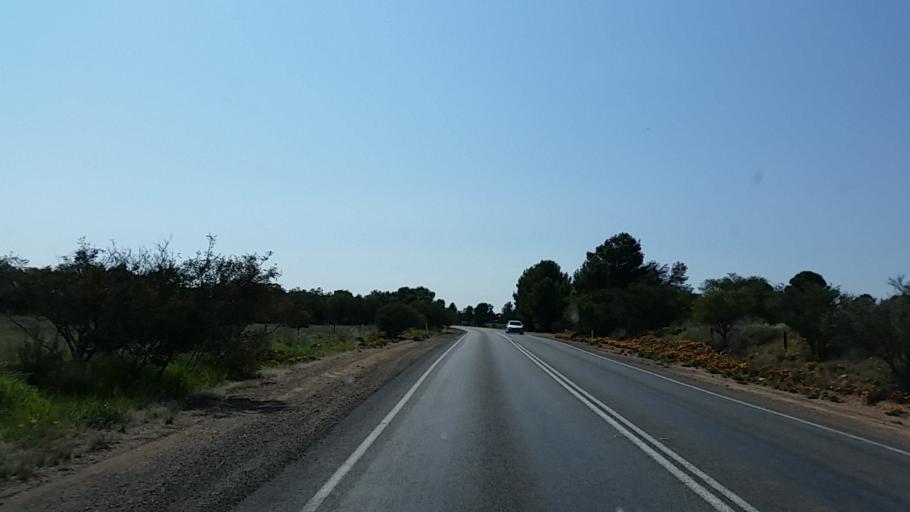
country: AU
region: South Australia
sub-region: Port Pirie City and Dists
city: Crystal Brook
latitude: -33.2644
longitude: 138.3476
